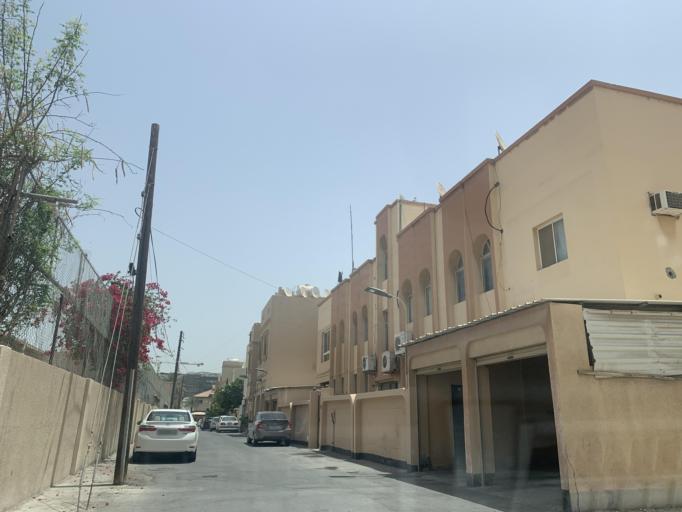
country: BH
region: Northern
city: Madinat `Isa
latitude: 26.1578
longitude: 50.5220
